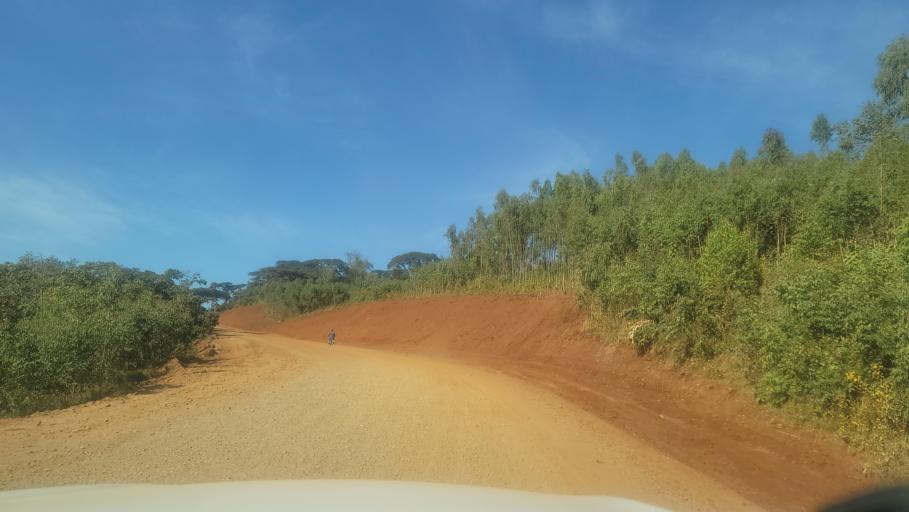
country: ET
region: Oromiya
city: Agaro
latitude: 7.8189
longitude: 36.5255
